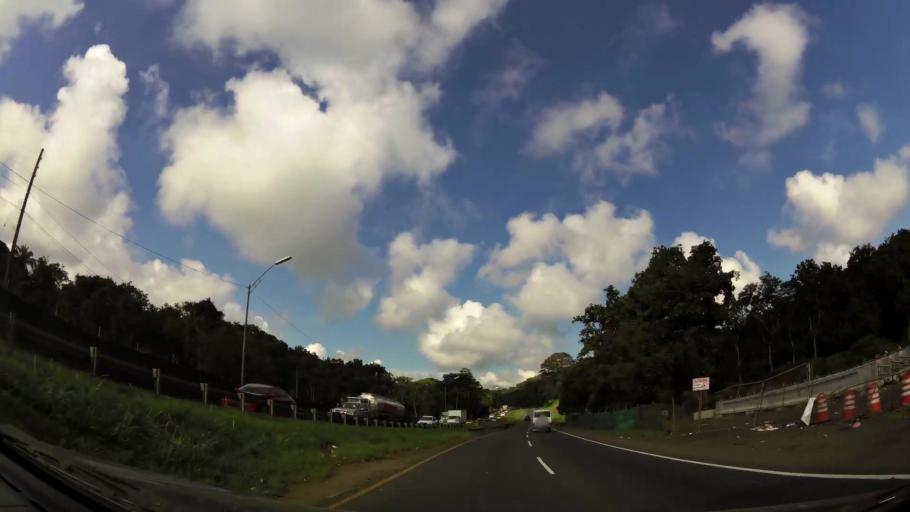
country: PA
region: Panama
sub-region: Distrito Arraijan
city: Arraijan
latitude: 8.9562
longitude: -79.6020
